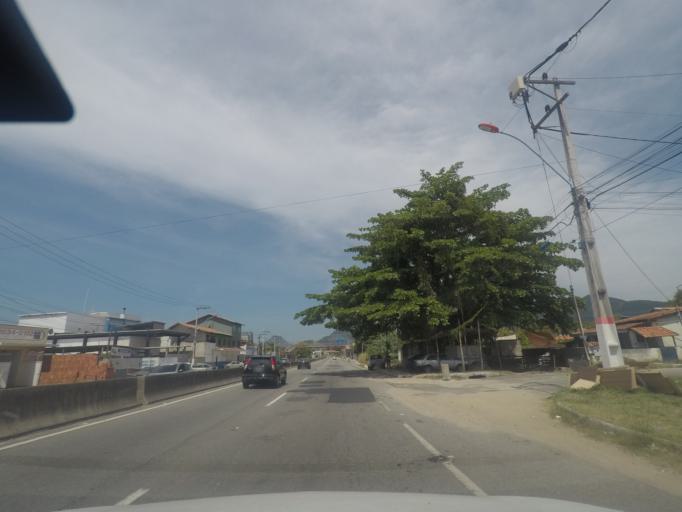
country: BR
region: Rio de Janeiro
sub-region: Marica
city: Marica
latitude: -22.9084
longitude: -42.8340
